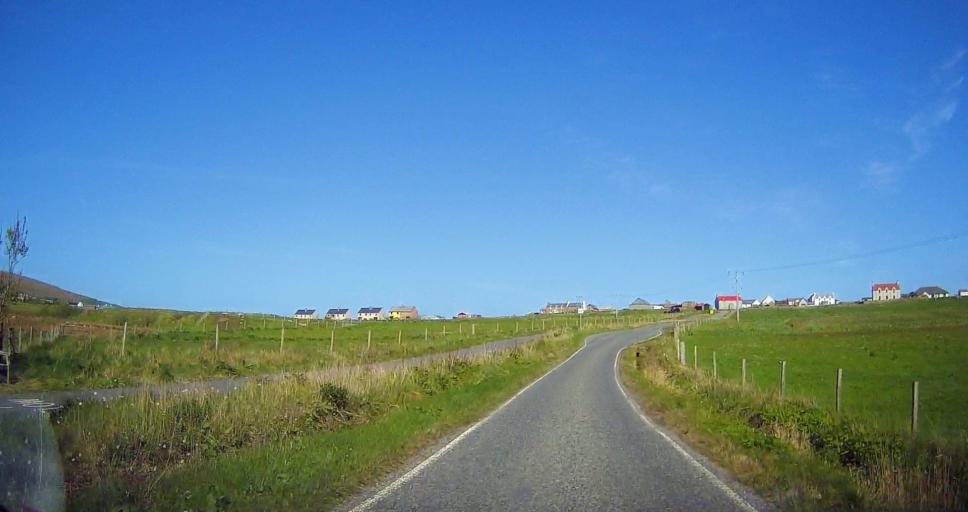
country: GB
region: Scotland
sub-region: Shetland Islands
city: Sandwick
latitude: 59.9990
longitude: -1.2532
